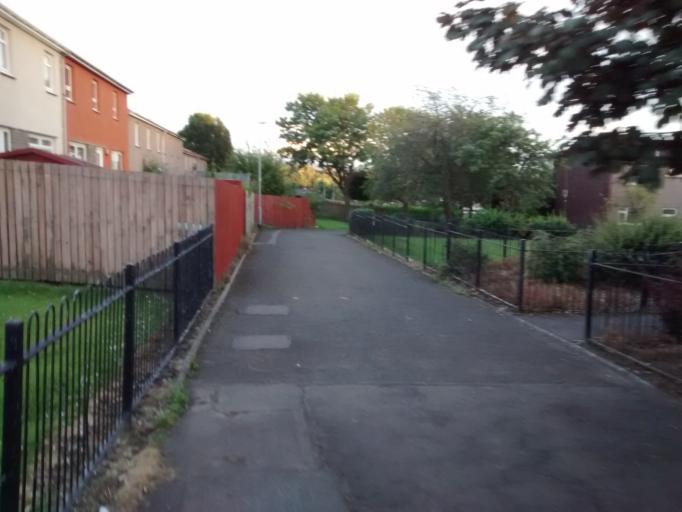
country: GB
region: Scotland
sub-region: West Lothian
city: Livingston
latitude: 55.8976
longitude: -3.5205
